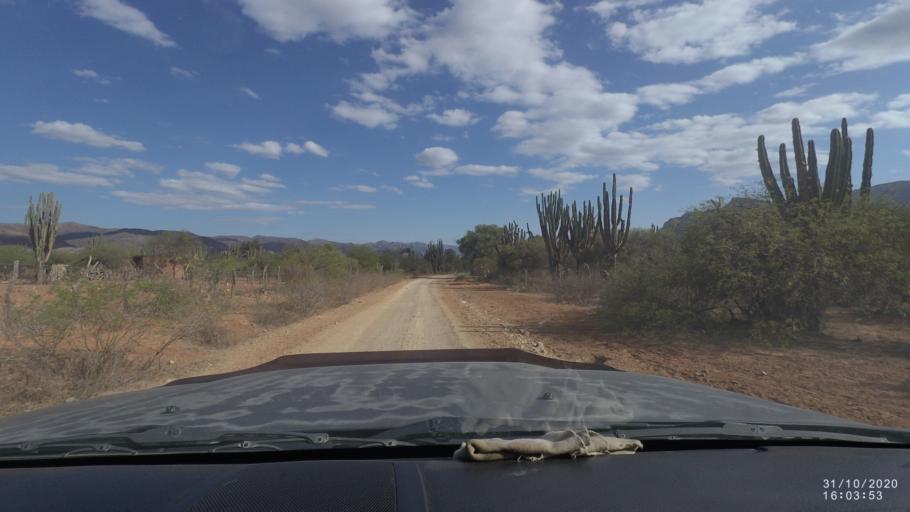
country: BO
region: Chuquisaca
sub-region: Provincia Zudanez
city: Mojocoya
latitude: -18.3556
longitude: -64.6512
